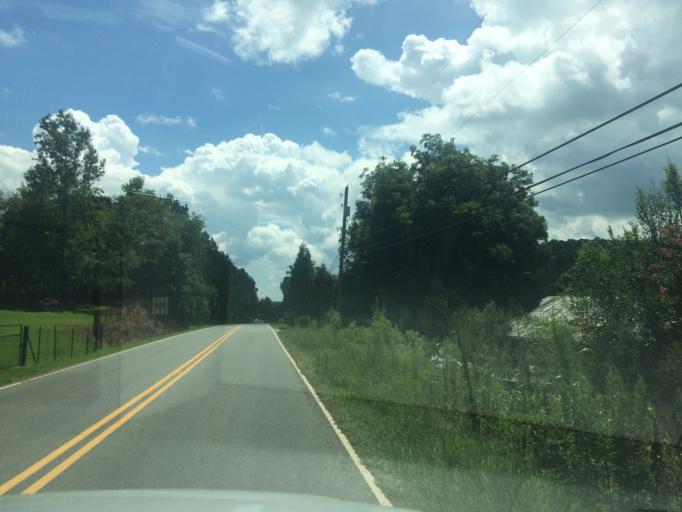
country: US
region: North Carolina
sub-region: Polk County
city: Columbus
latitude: 35.2973
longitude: -82.1611
